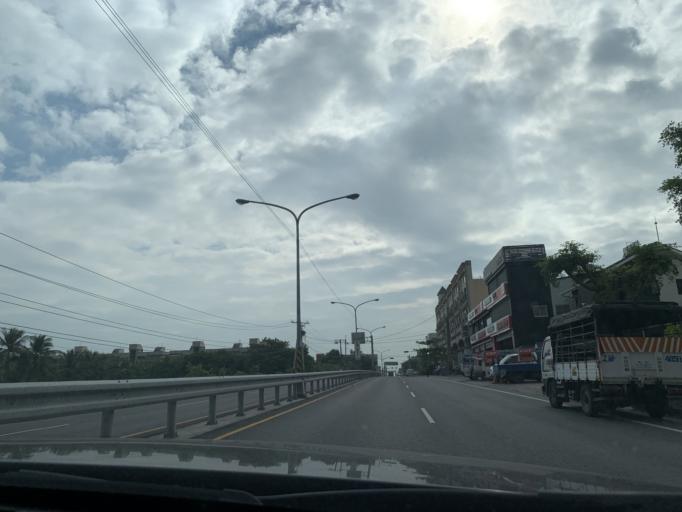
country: TW
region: Taiwan
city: Fengshan
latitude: 22.4652
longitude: 120.4629
